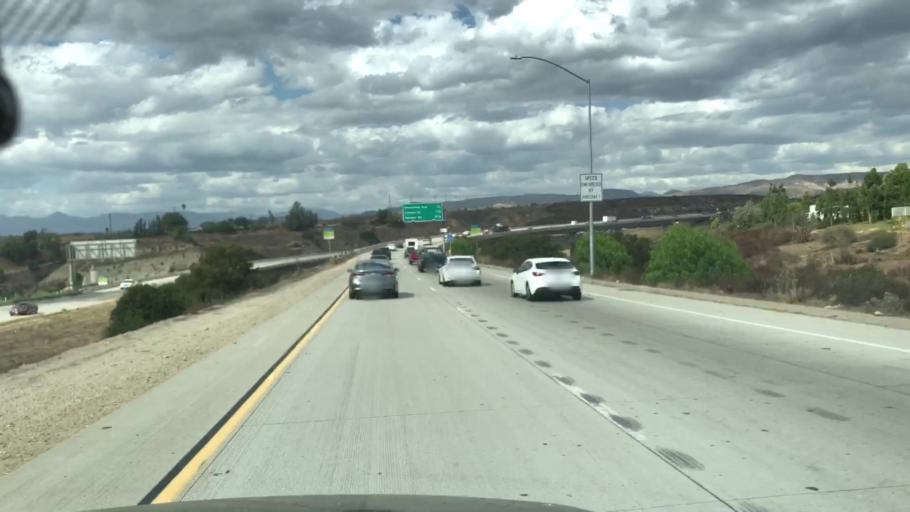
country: US
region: California
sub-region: Ventura County
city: Moorpark
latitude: 34.2839
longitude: -118.8636
